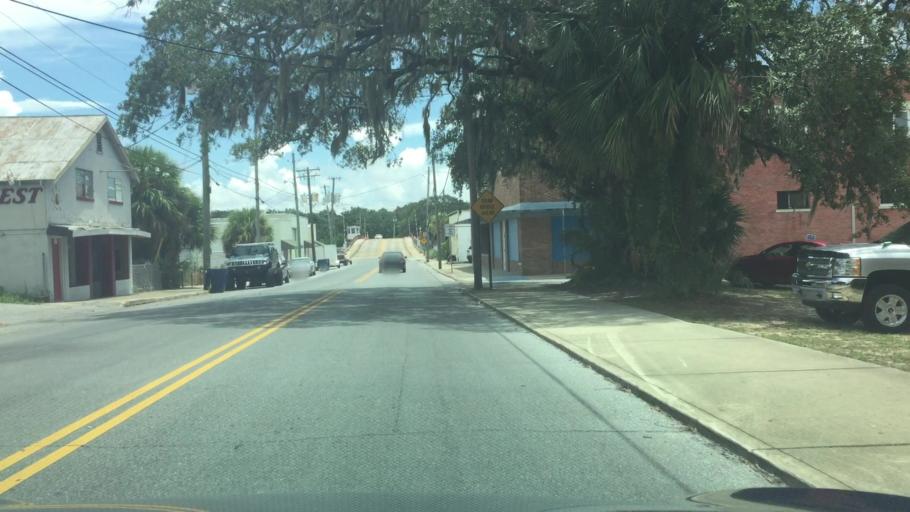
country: US
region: Florida
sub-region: Bay County
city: Panama City
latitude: 30.1526
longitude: -85.6611
